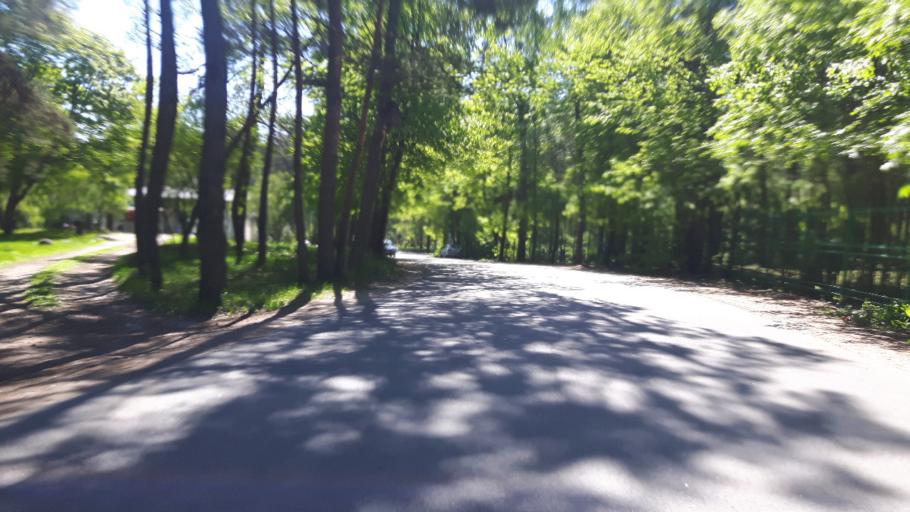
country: RU
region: St.-Petersburg
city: Zelenogorsk
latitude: 60.1948
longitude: 29.6660
